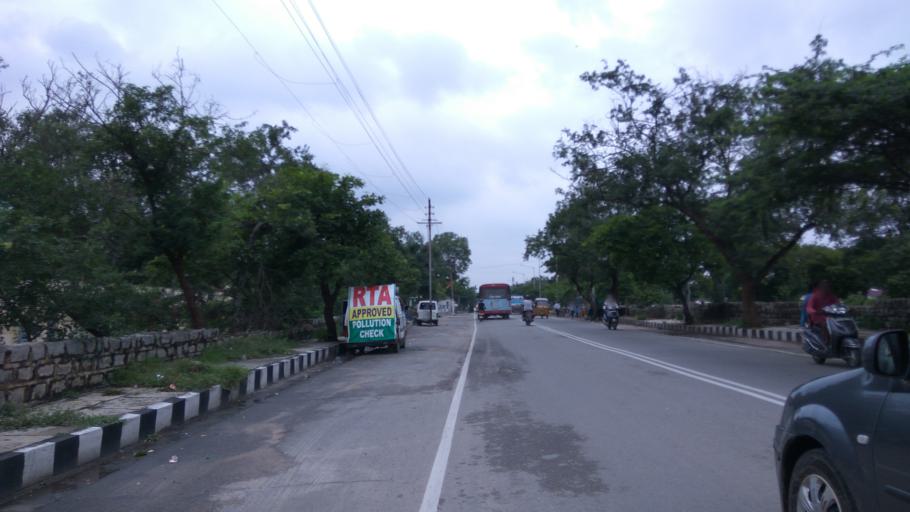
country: IN
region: Telangana
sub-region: Hyderabad
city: Malkajgiri
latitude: 17.4392
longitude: 78.5274
